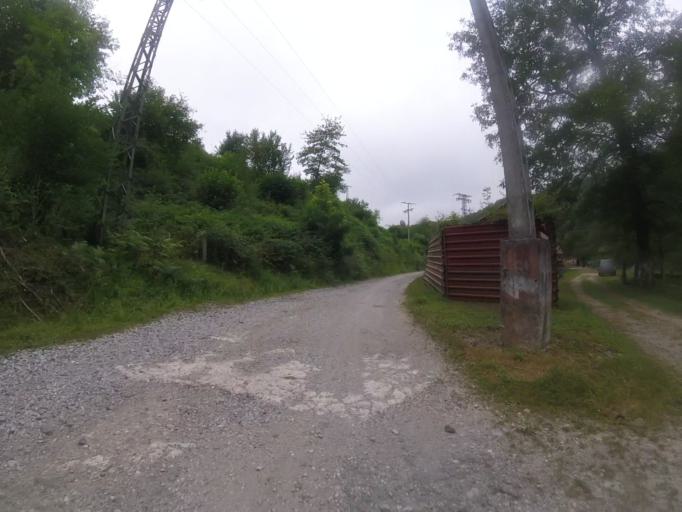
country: ES
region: Navarre
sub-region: Provincia de Navarra
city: Areso
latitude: 43.1118
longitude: -1.9361
